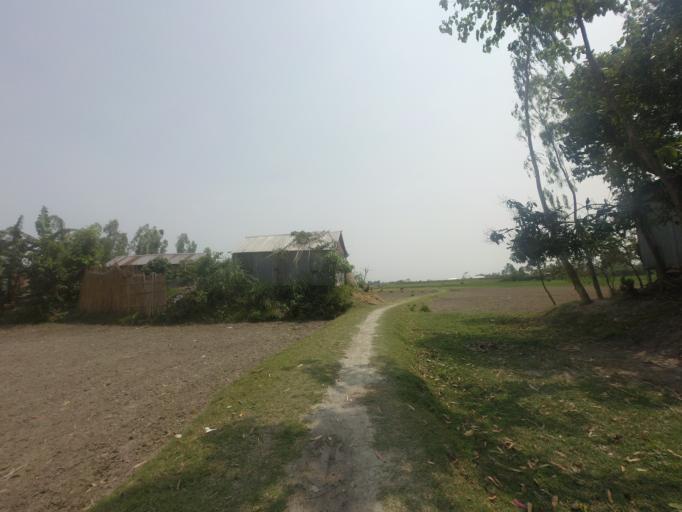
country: BD
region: Rajshahi
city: Sirajganj
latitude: 24.3562
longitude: 89.7222
